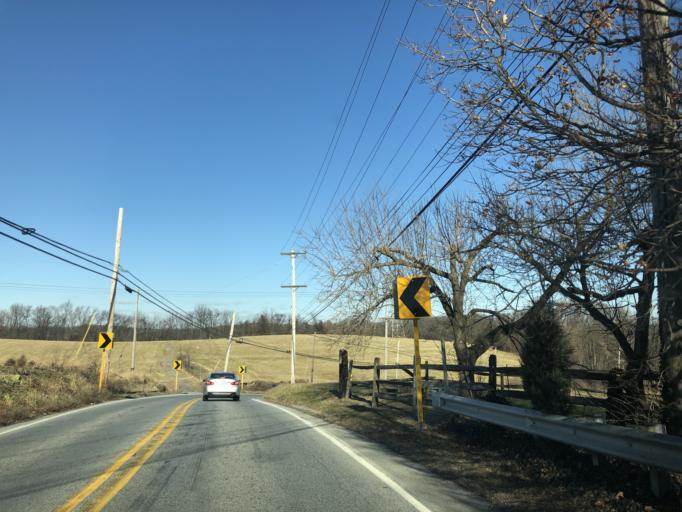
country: US
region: Pennsylvania
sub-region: Chester County
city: South Coatesville
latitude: 39.9656
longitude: -75.8359
